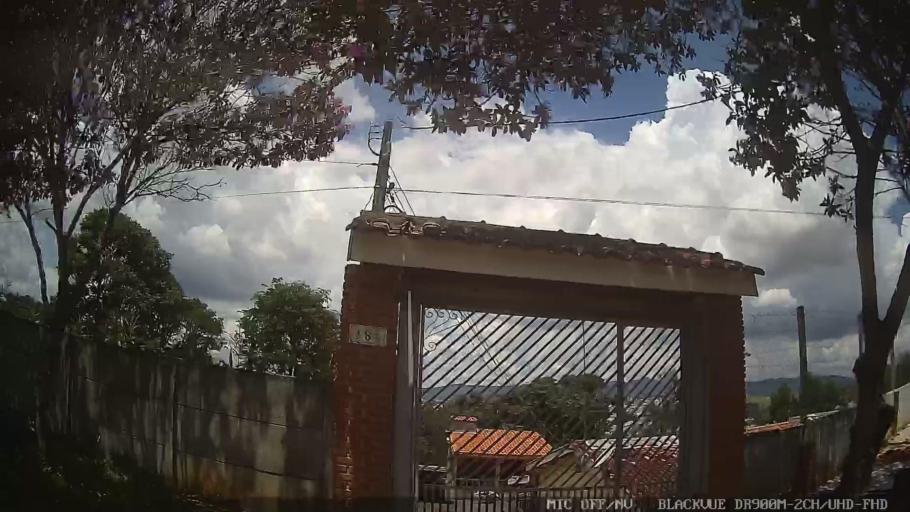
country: BR
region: Sao Paulo
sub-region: Atibaia
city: Atibaia
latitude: -23.1227
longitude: -46.6036
